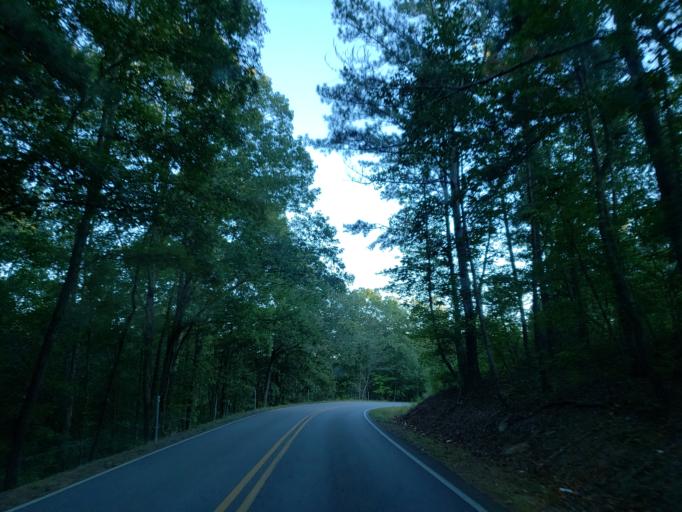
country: US
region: Georgia
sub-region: Bartow County
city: Rydal
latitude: 34.3533
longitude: -84.5801
